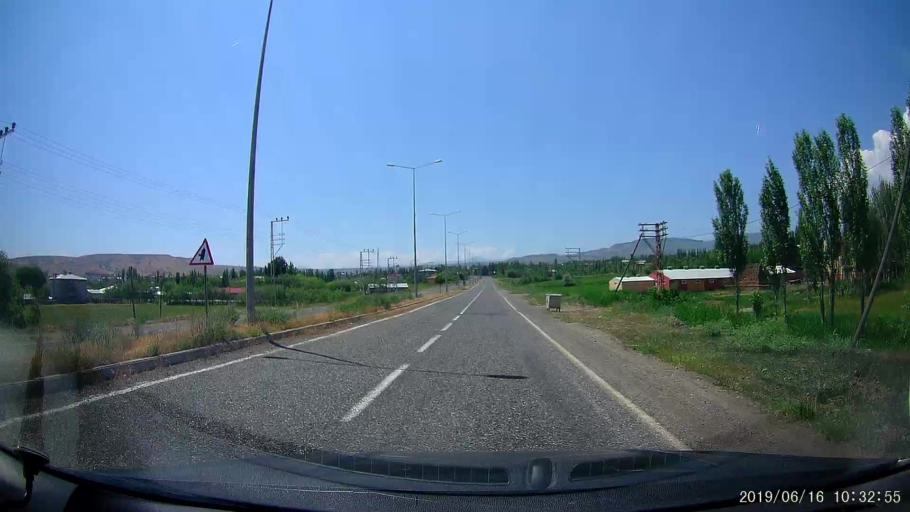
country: TR
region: Igdir
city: Tuzluca
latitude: 40.0459
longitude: 43.6542
